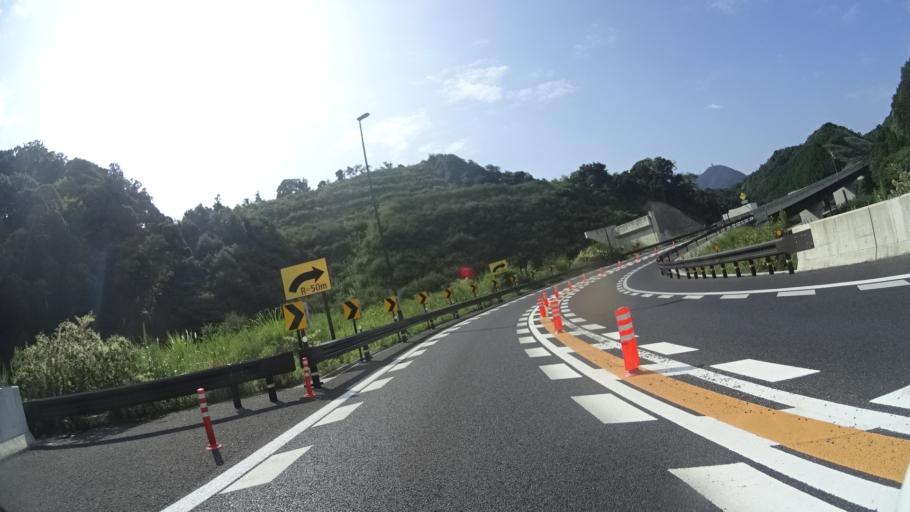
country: JP
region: Shimane
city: Odacho-oda
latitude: 35.1427
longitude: 132.4132
